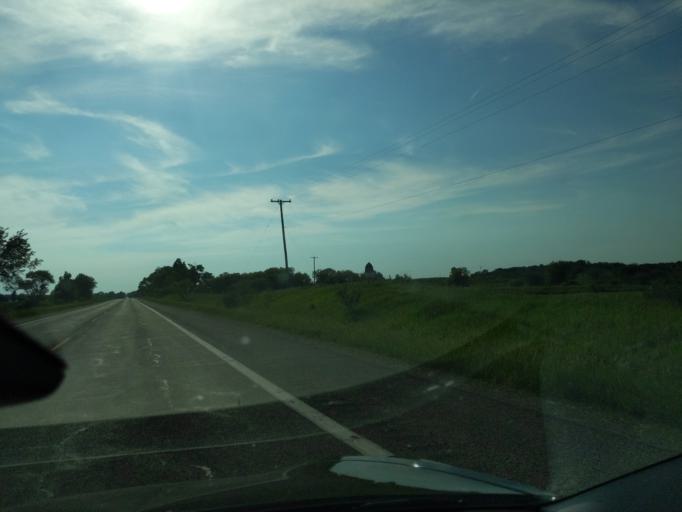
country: US
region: Michigan
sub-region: Barry County
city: Nashville
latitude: 42.6035
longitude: -85.1408
